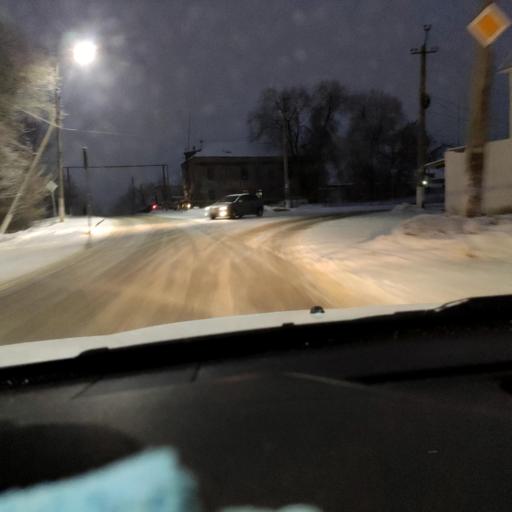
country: RU
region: Samara
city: Smyshlyayevka
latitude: 53.2494
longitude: 50.4819
